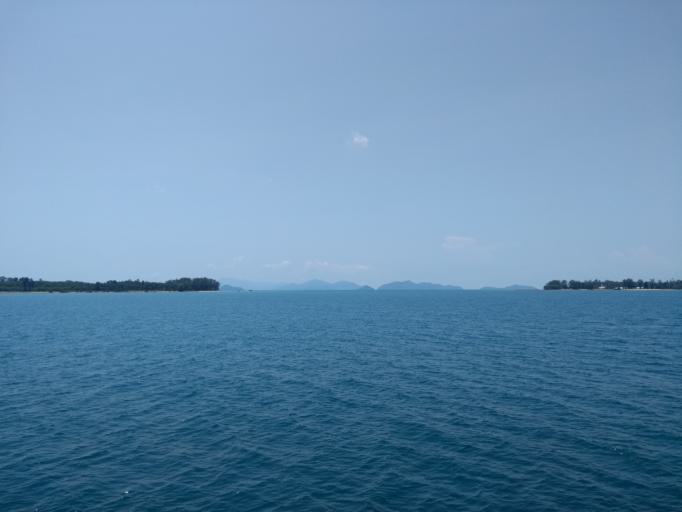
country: TH
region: Trat
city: Ko Kut
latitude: 11.8149
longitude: 102.5216
